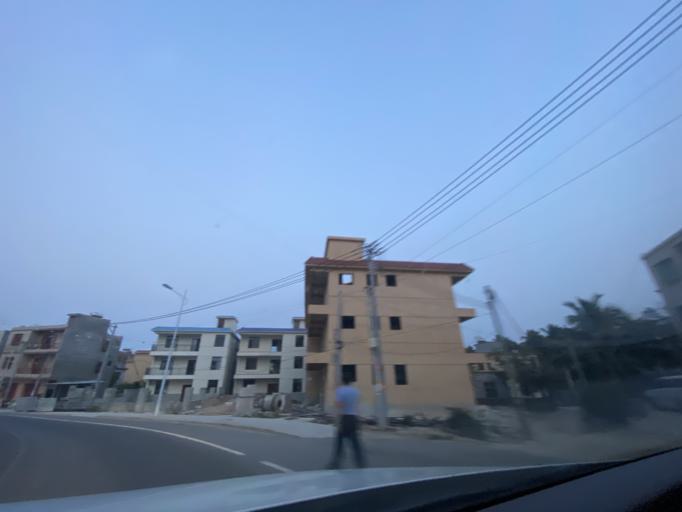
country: CN
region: Hainan
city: Yingzhou
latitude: 18.4068
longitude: 109.8638
